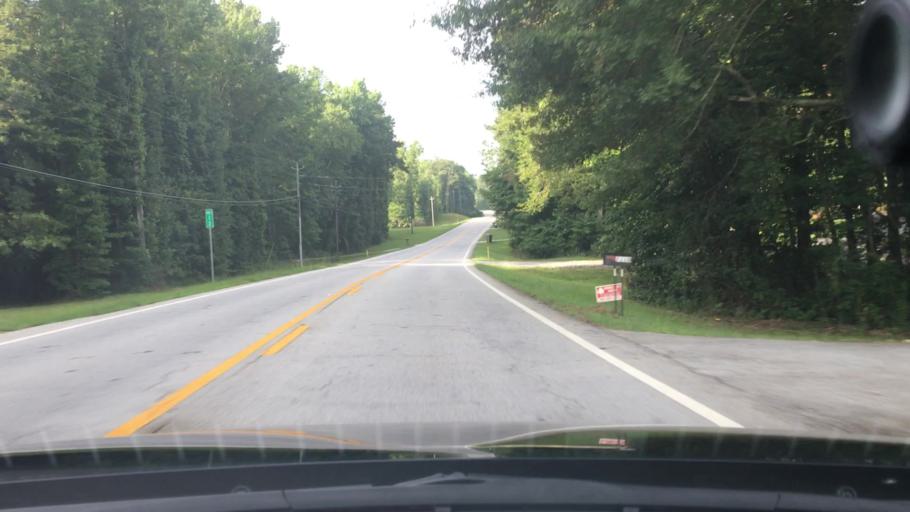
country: US
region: Georgia
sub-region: Fayette County
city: Peachtree City
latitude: 33.3540
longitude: -84.6373
